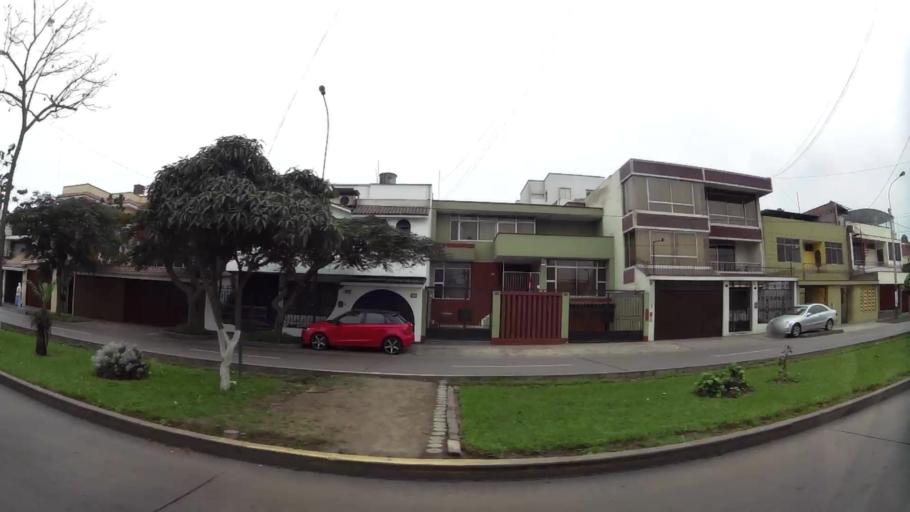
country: PE
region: Lima
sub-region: Lima
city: San Luis
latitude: -12.0852
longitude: -77.0175
